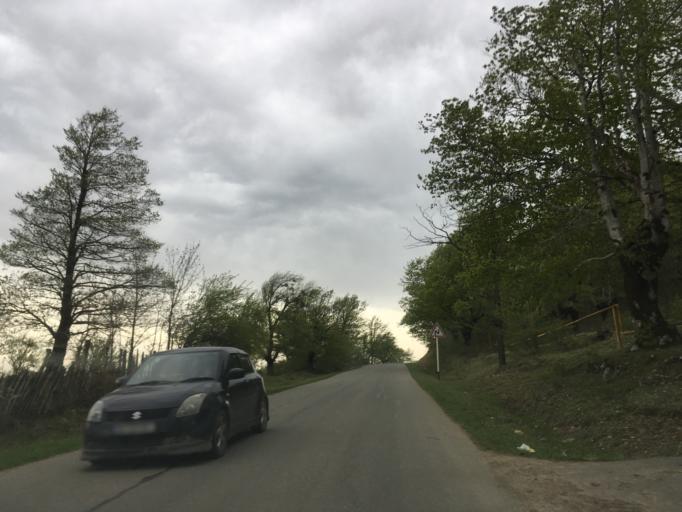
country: GE
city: Surami
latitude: 42.2157
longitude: 43.4244
